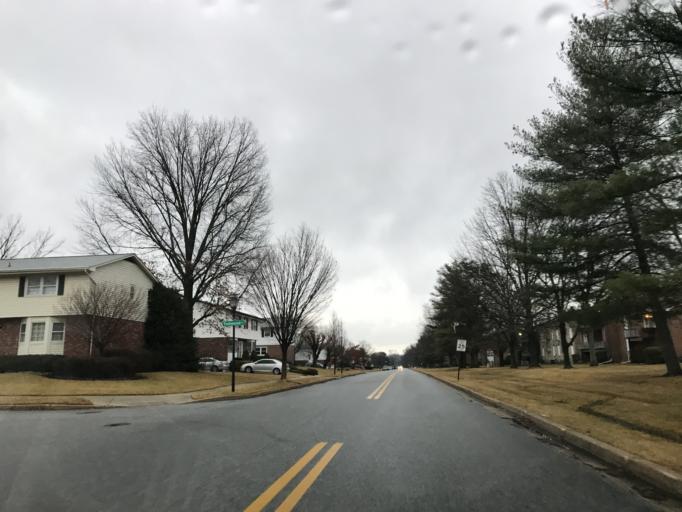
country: US
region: Maryland
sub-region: Baltimore County
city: Pikesville
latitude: 39.3720
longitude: -76.6918
